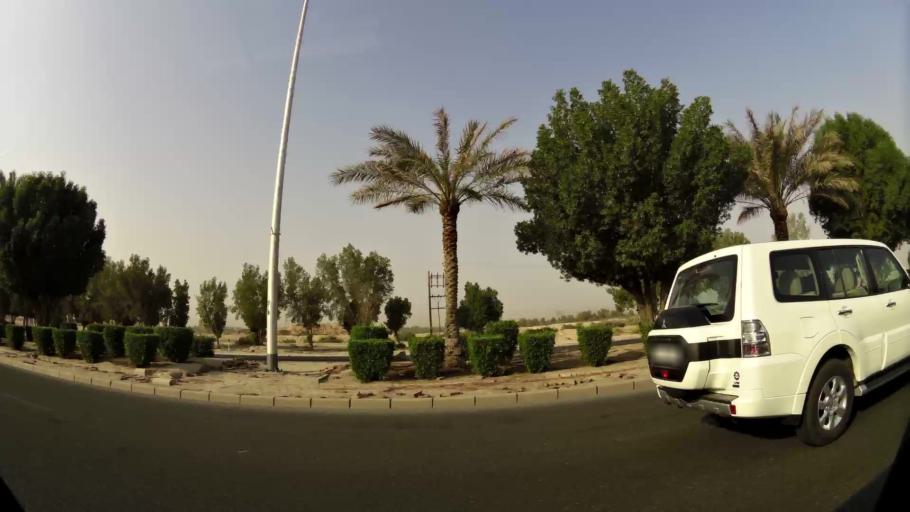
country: KW
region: Al Asimah
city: Ar Rabiyah
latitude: 29.3174
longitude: 47.8053
